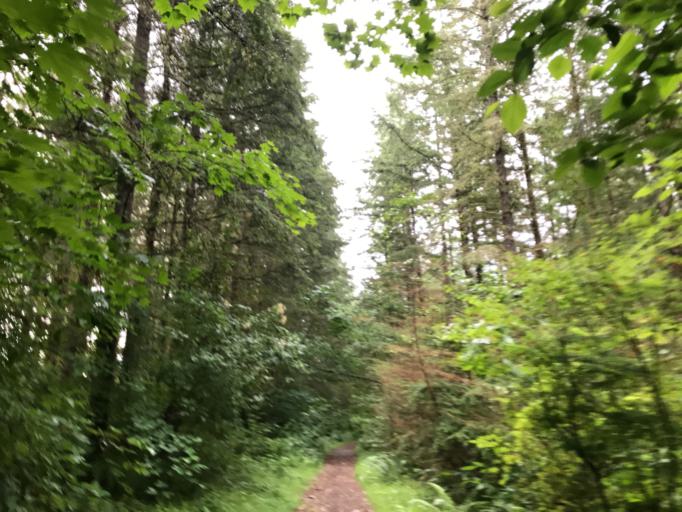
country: US
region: Washington
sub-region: King County
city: Ravensdale
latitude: 47.3470
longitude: -122.0077
